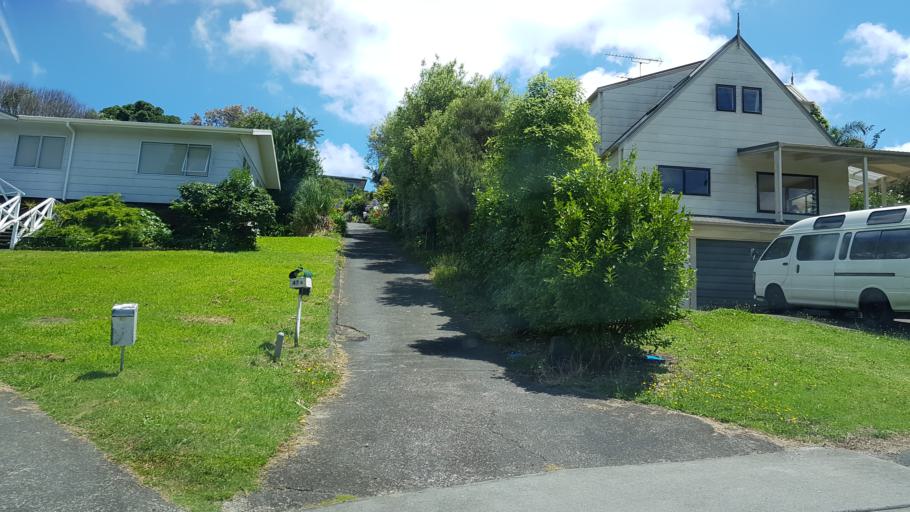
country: NZ
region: Auckland
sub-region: Auckland
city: North Shore
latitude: -36.7899
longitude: 174.7244
